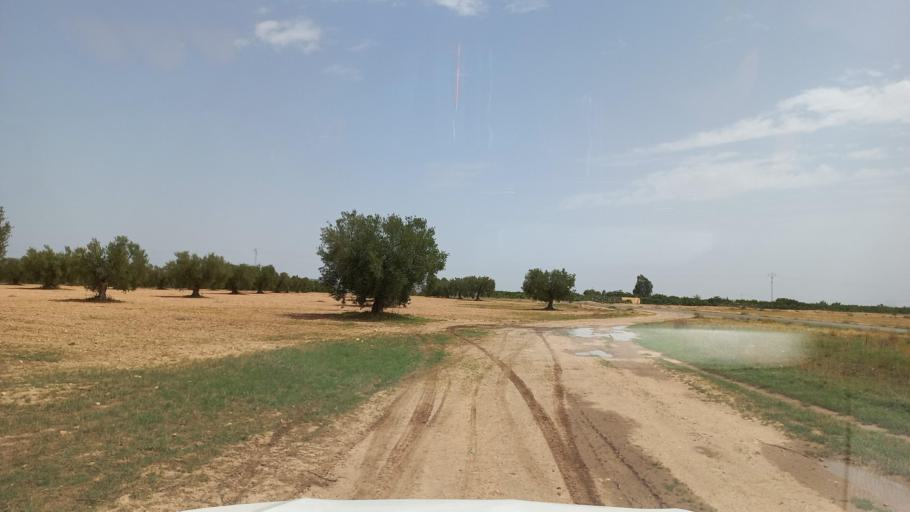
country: TN
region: Al Qasrayn
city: Kasserine
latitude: 35.2872
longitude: 9.0329
